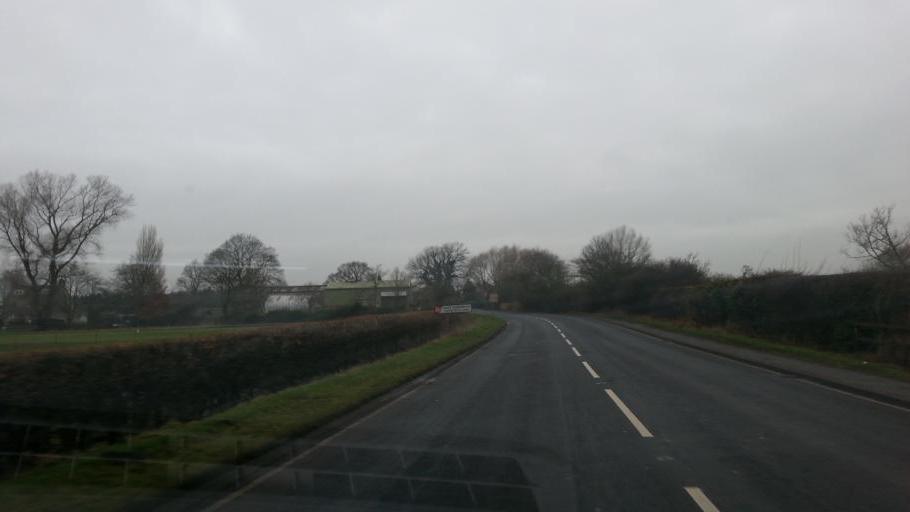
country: GB
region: England
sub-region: City and Borough of Wakefield
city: Badsworth
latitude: 53.6453
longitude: -1.2848
